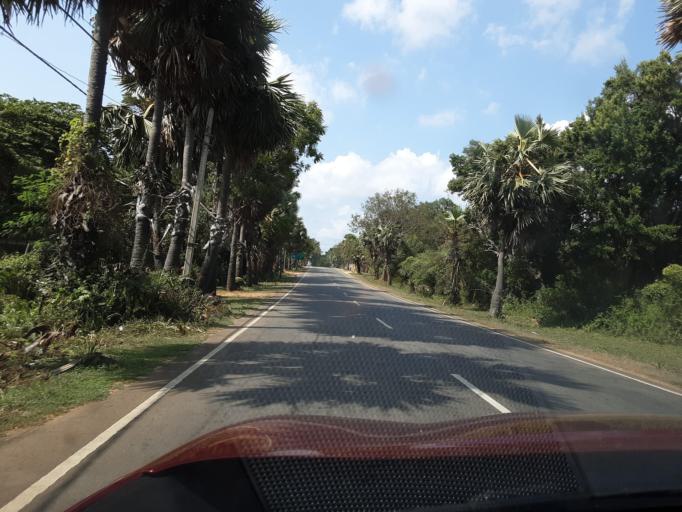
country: LK
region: Southern
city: Tangalla
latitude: 6.2694
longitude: 81.2269
